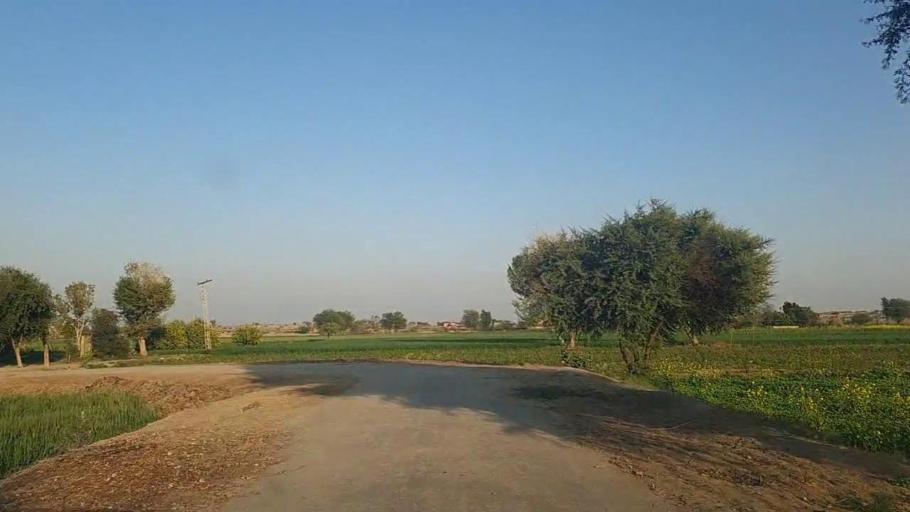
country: PK
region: Sindh
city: Jam Sahib
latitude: 26.3488
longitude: 68.6759
